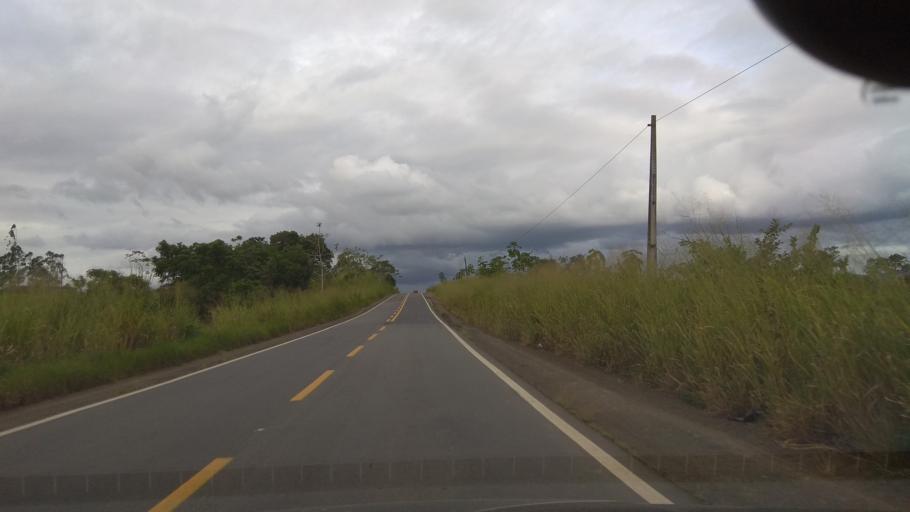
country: BR
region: Bahia
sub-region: Ipiau
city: Ipiau
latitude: -14.1947
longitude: -39.6406
